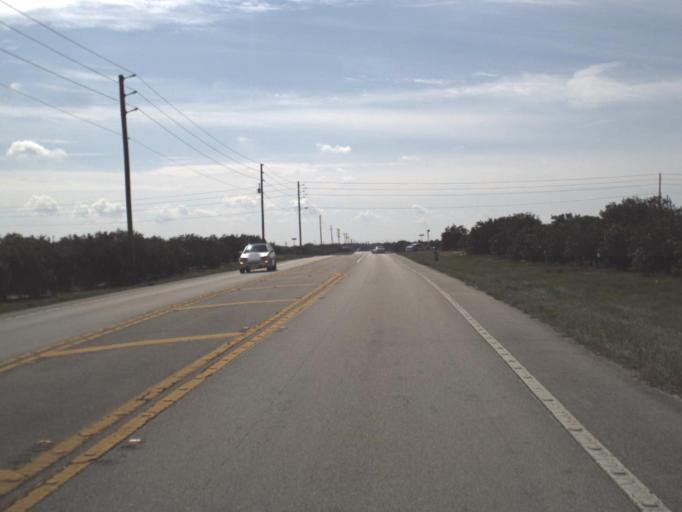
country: US
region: Florida
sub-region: Highlands County
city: Sebring
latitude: 27.5310
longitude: -81.4535
